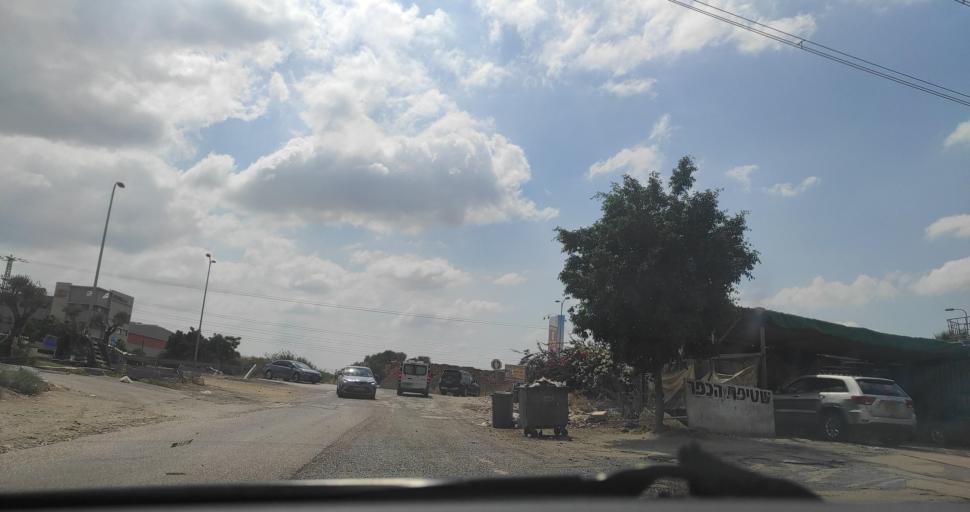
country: IL
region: Central District
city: Rosh Ha'Ayin
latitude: 32.1125
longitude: 34.9549
